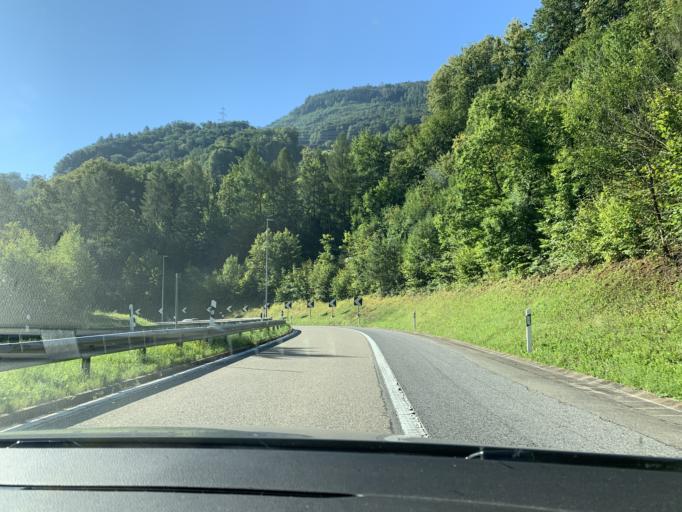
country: CH
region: Saint Gallen
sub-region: Wahlkreis Sarganserland
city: Quarten
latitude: 47.1139
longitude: 9.1904
